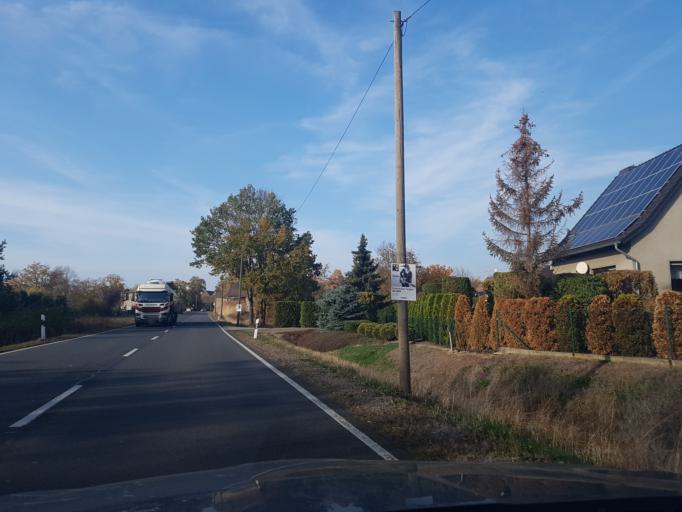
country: DE
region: Saxony
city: Beilrode
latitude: 51.5530
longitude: 13.0365
